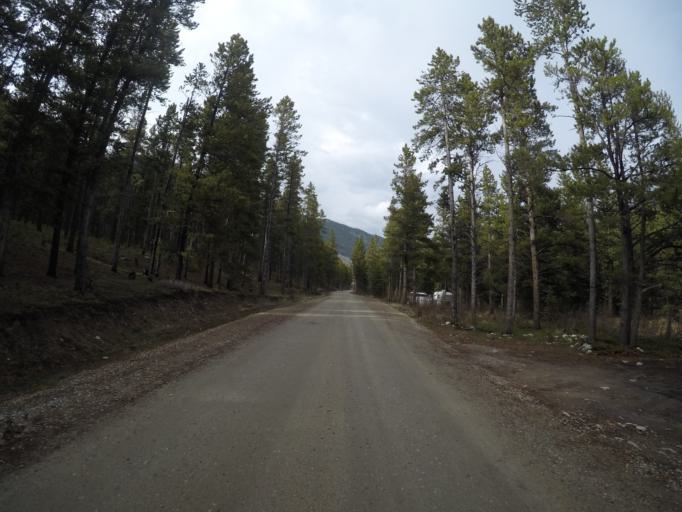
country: US
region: Montana
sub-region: Carbon County
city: Red Lodge
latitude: 45.0487
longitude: -109.4237
